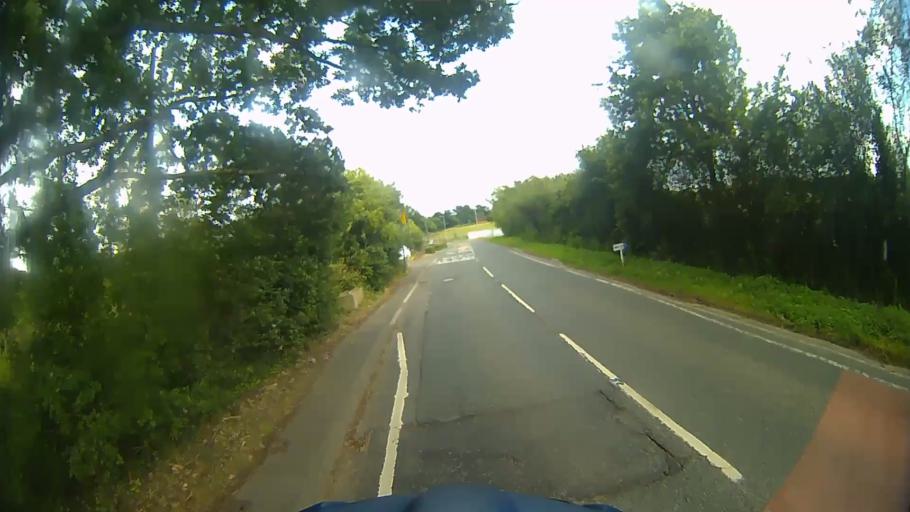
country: GB
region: England
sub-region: Wokingham
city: Barkham
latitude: 51.3958
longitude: -0.8866
